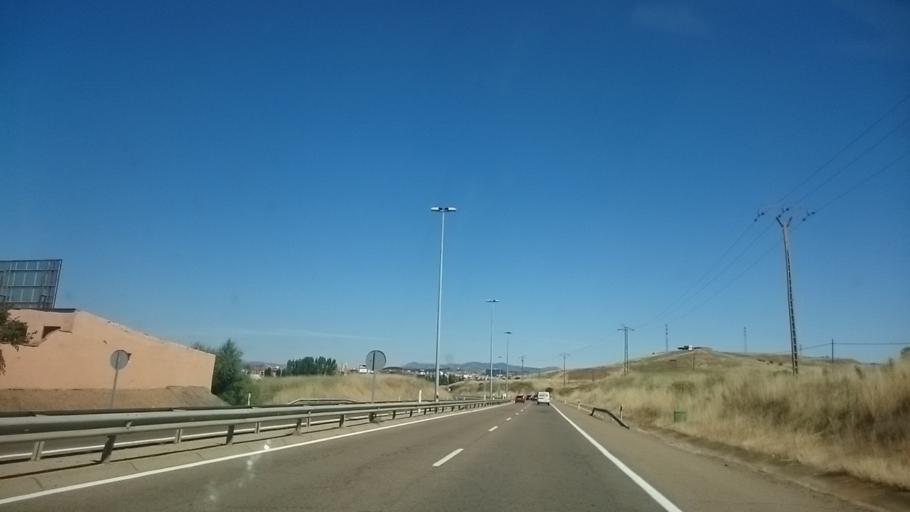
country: ES
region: Castille and Leon
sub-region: Provincia de Leon
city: Leon
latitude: 42.5817
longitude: -5.5468
